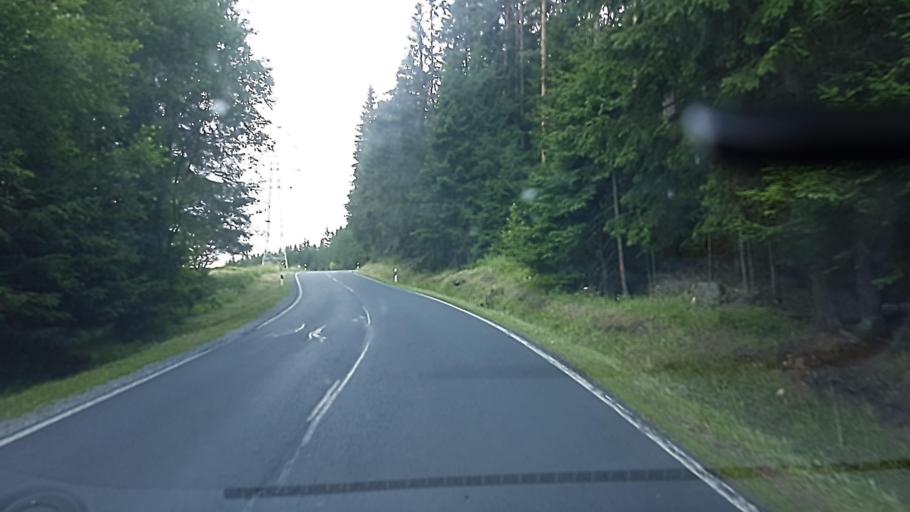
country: DE
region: Bavaria
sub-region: Upper Palatinate
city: Brand
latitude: 49.9700
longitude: 11.8839
